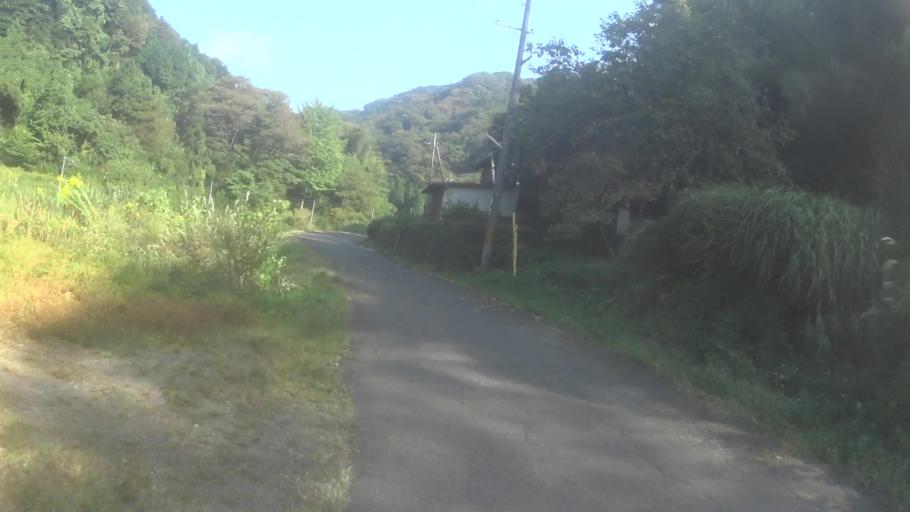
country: JP
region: Kyoto
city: Miyazu
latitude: 35.7140
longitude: 135.1281
